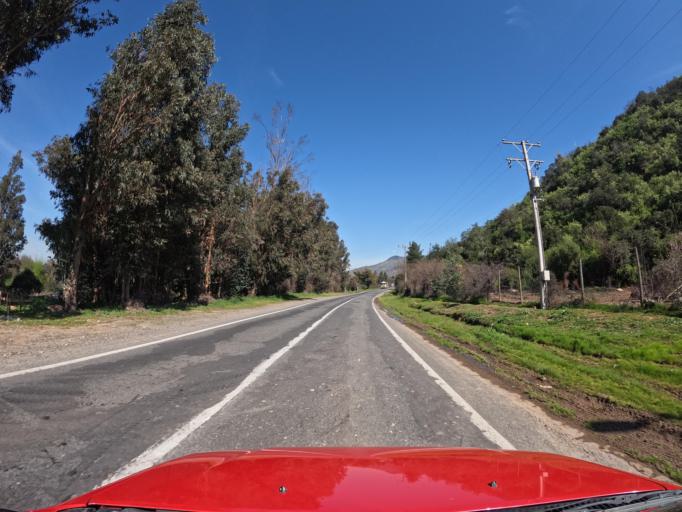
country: CL
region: Maule
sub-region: Provincia de Curico
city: Rauco
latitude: -35.0526
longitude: -71.6041
